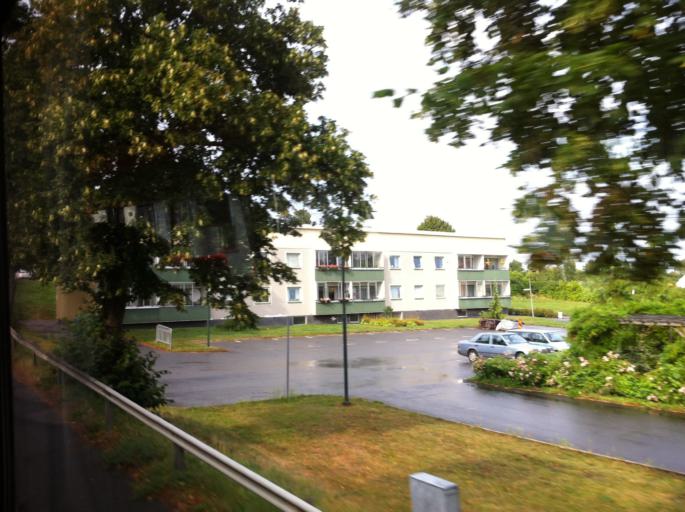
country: SE
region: Skane
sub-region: Kristianstads Kommun
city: Degeberga
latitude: 55.8399
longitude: 14.0904
